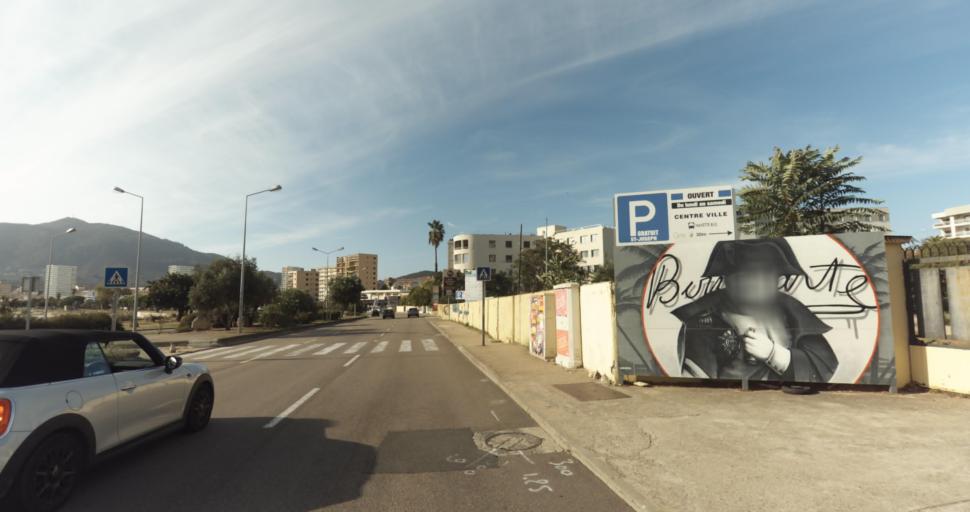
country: FR
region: Corsica
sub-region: Departement de la Corse-du-Sud
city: Ajaccio
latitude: 41.9319
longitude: 8.7566
